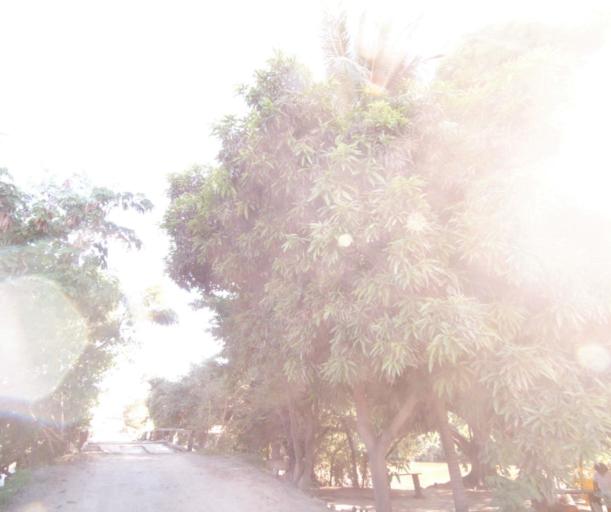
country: BR
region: Minas Gerais
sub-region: Manga
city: Manga
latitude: -14.3127
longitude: -44.4612
